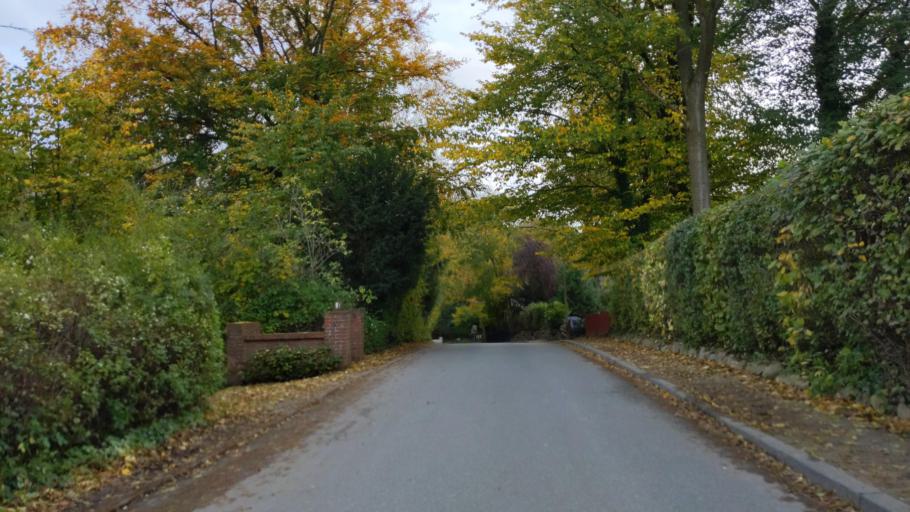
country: DE
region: Schleswig-Holstein
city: Susel
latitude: 54.0417
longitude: 10.7067
